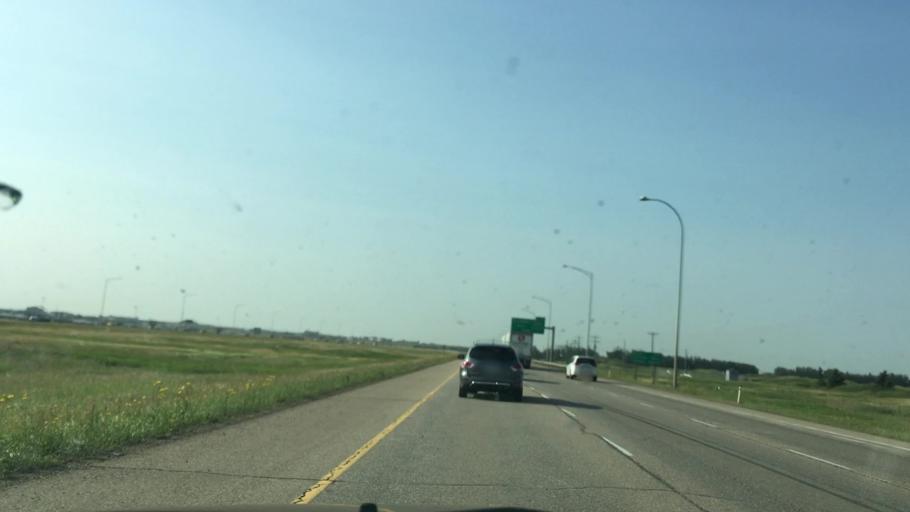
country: CA
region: Alberta
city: Leduc
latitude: 53.3319
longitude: -113.5499
